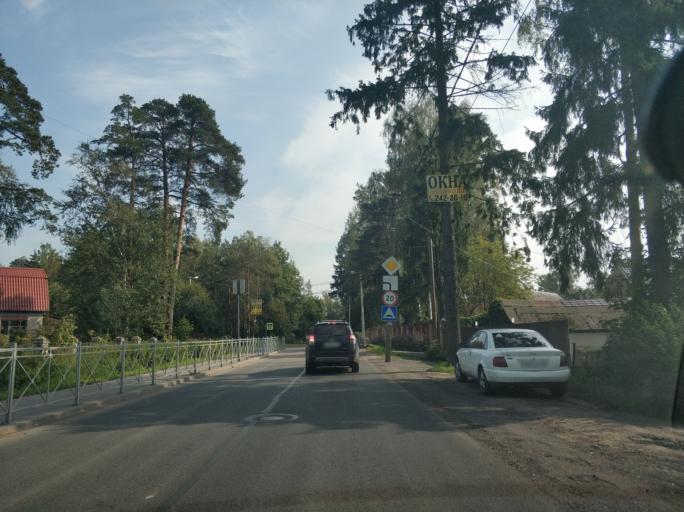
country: RU
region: Leningrad
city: Vsevolozhsk
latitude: 60.0191
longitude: 30.6745
